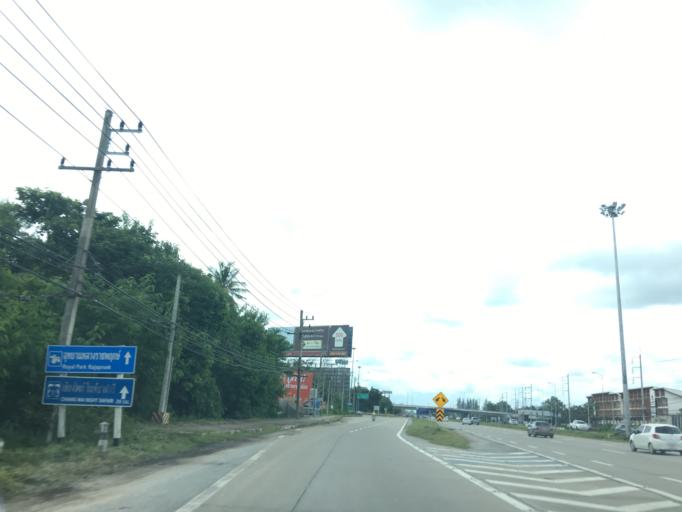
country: TH
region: Chiang Mai
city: Saraphi
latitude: 18.7569
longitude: 99.0311
